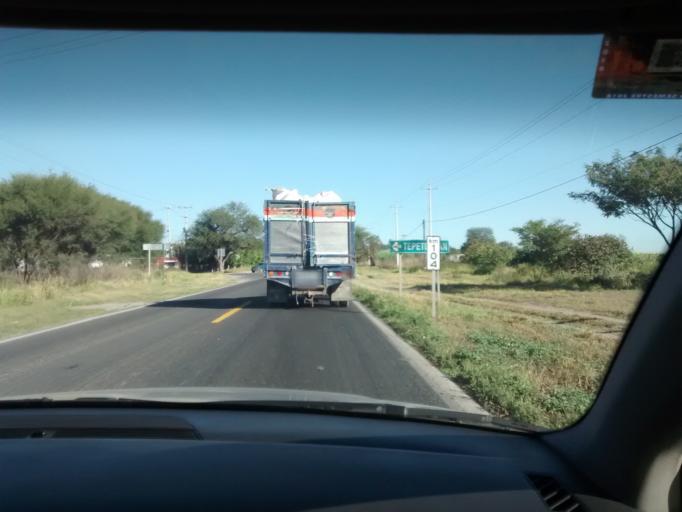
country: MX
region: Puebla
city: San Bartolo Teontepec
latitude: 18.5311
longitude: -97.5225
